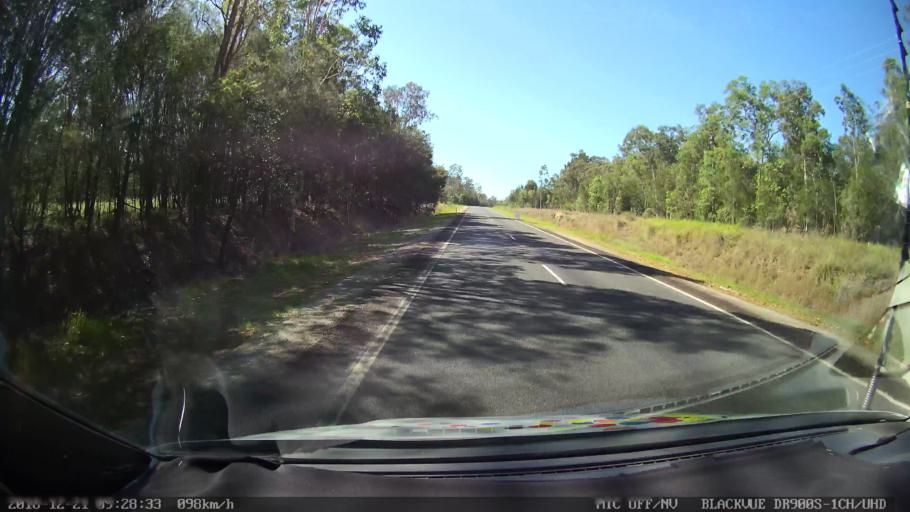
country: AU
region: New South Wales
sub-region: Clarence Valley
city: Maclean
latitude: -29.4191
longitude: 152.9872
